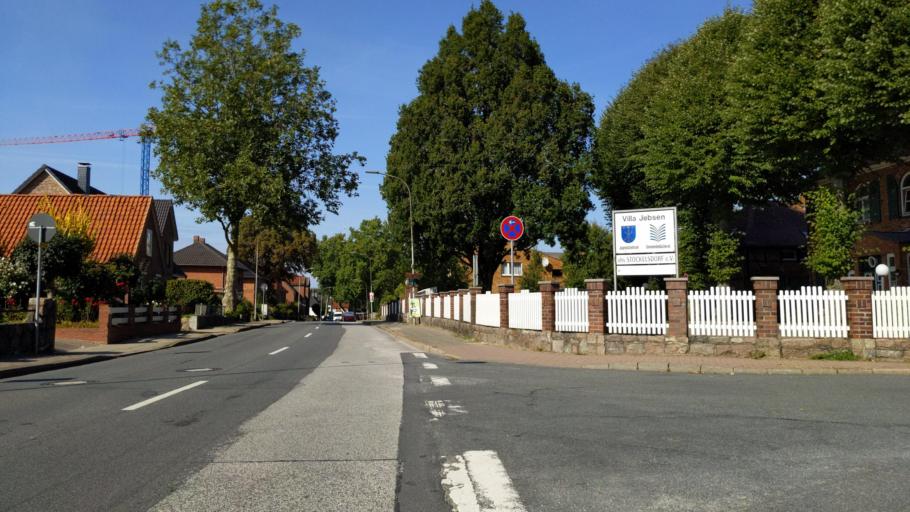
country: DE
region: Schleswig-Holstein
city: Stockelsdorf
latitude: 53.8947
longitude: 10.6476
